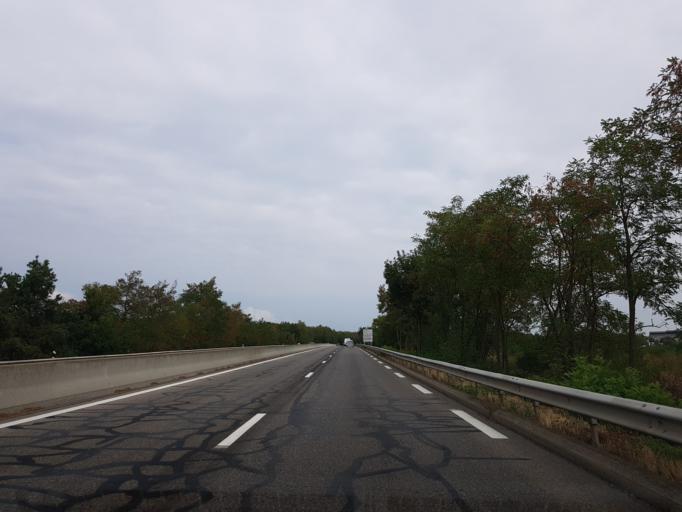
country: FR
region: Alsace
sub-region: Departement du Haut-Rhin
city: Bollwiller
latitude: 47.8416
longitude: 7.2769
